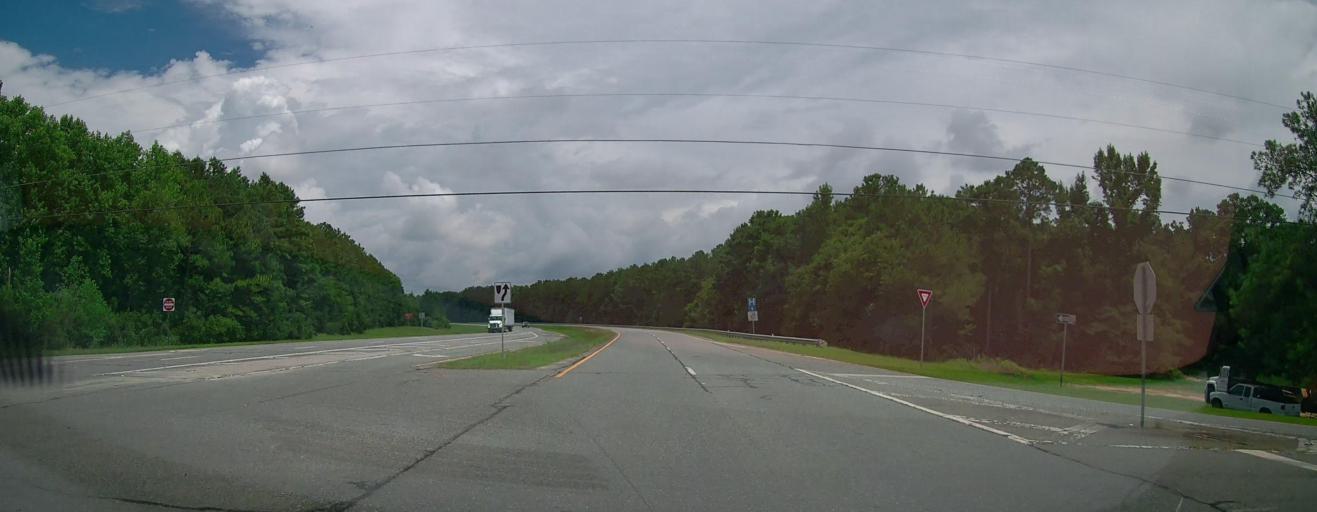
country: US
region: Georgia
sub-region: Dodge County
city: Eastman
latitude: 32.1808
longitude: -83.1925
